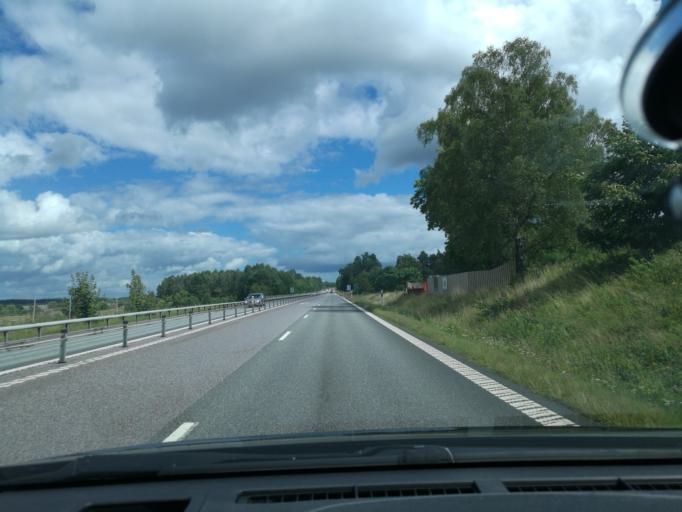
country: SE
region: Skane
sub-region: Hassleholms Kommun
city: Hastveda
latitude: 56.2465
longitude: 13.9146
